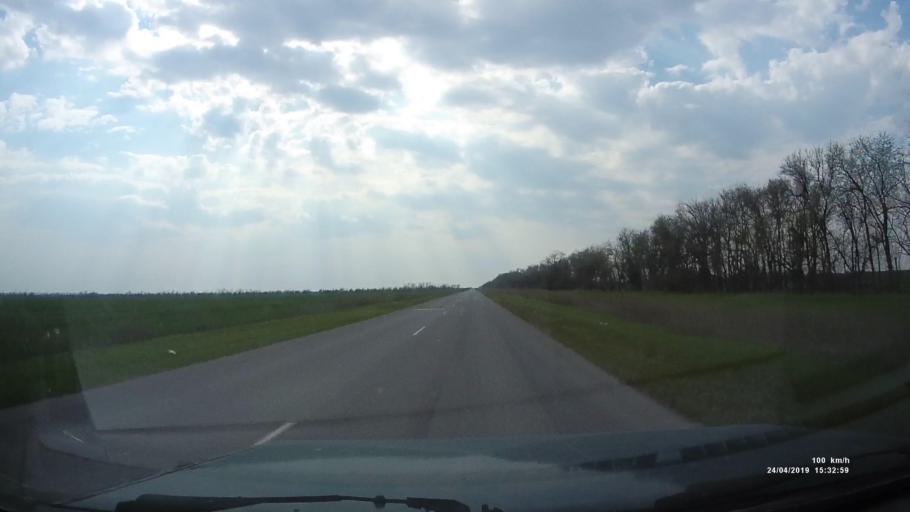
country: RU
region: Rostov
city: Remontnoye
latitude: 46.5995
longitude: 42.9484
